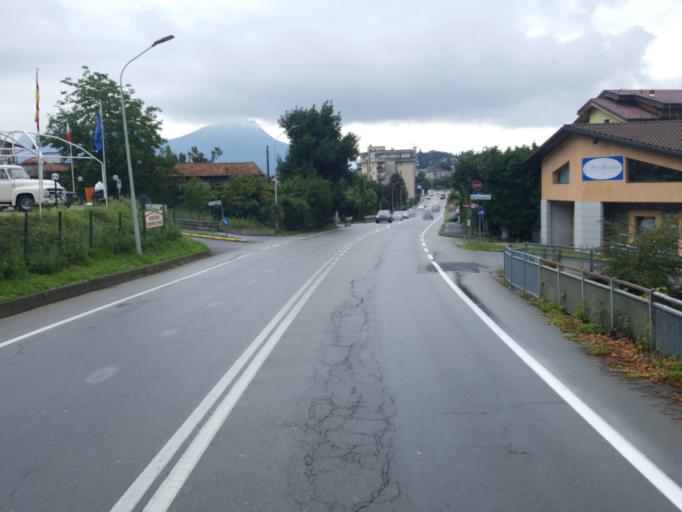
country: IT
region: Piedmont
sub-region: Provincia Verbano-Cusio-Ossola
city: Verbania
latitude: 45.9321
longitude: 8.5421
